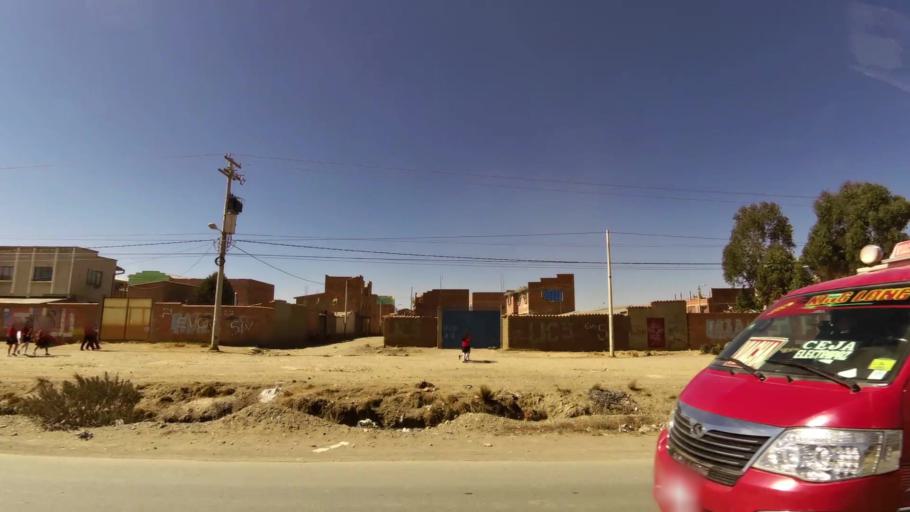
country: BO
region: La Paz
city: La Paz
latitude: -16.5725
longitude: -68.2257
